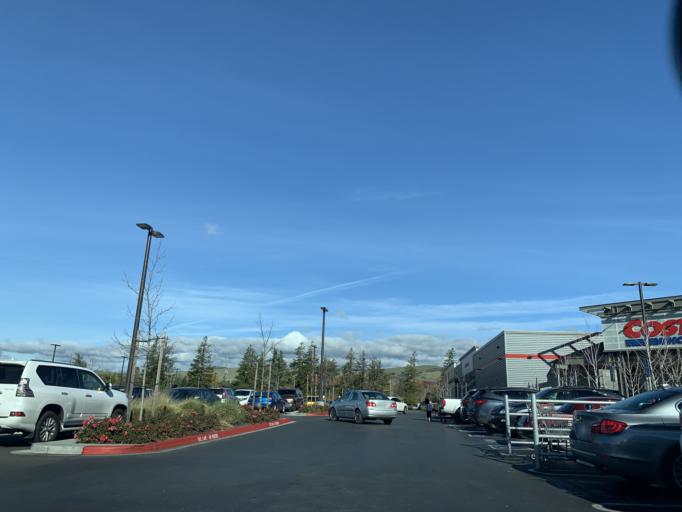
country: US
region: California
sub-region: Santa Clara County
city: Seven Trees
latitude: 37.2435
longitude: -121.7867
